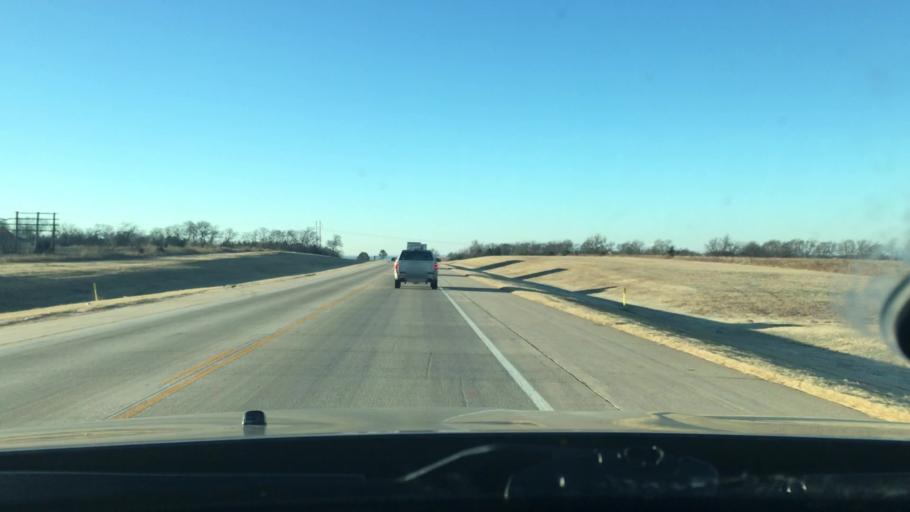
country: US
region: Oklahoma
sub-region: Murray County
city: Sulphur
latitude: 34.5166
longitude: -97.0074
